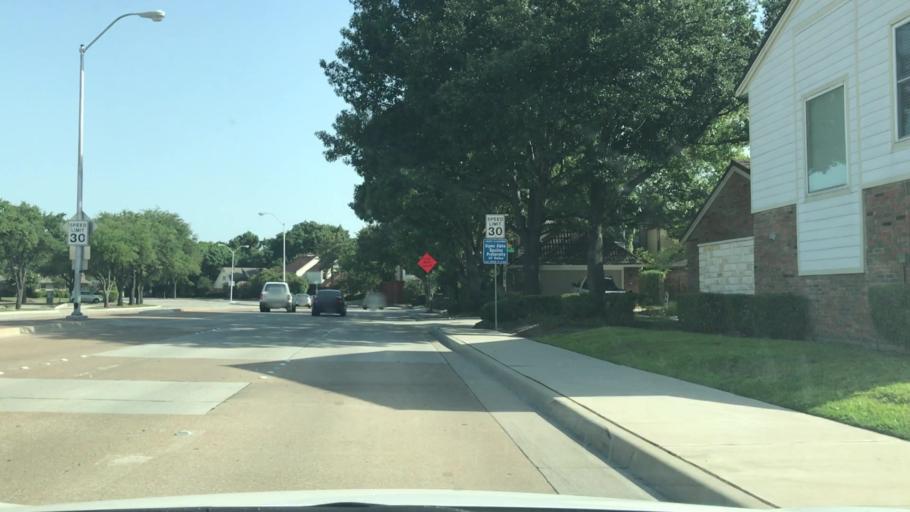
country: US
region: Texas
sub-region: Collin County
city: Plano
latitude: 33.0183
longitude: -96.7500
